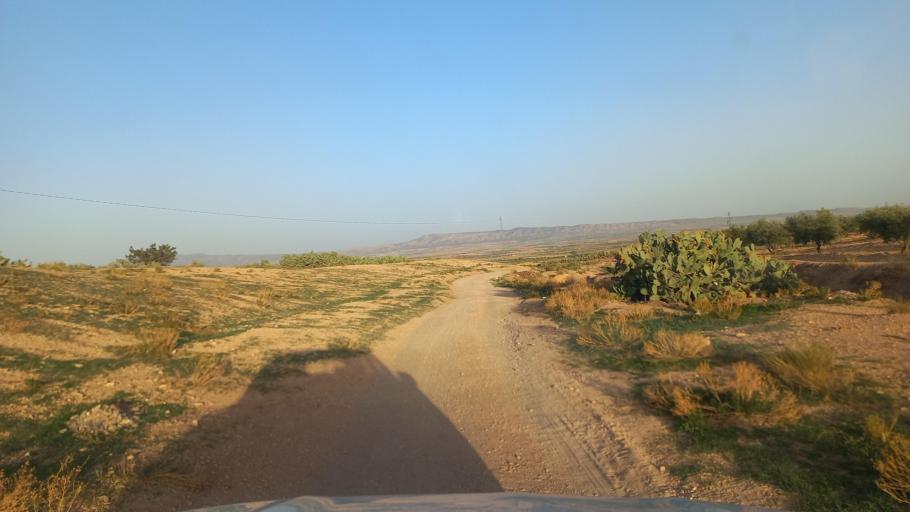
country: TN
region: Al Qasrayn
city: Sbiba
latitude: 35.3727
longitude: 9.0056
